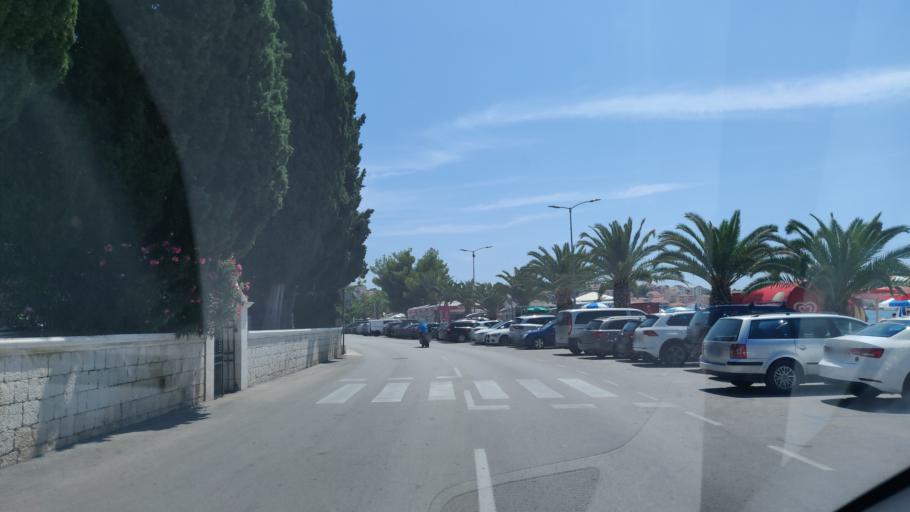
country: HR
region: Splitsko-Dalmatinska
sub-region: Grad Trogir
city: Trogir
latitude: 43.5004
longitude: 16.2593
